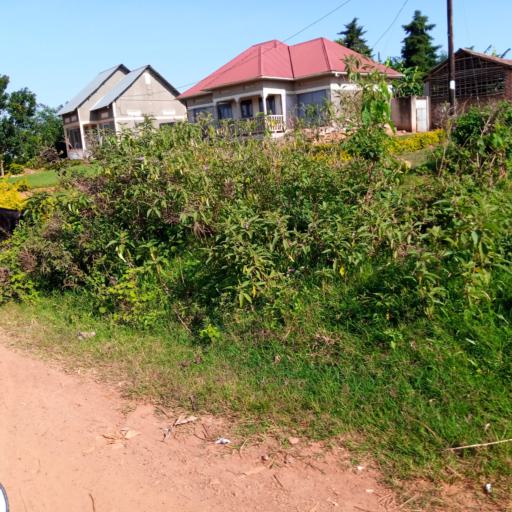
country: UG
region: Central Region
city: Masaka
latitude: -0.4370
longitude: 31.6660
